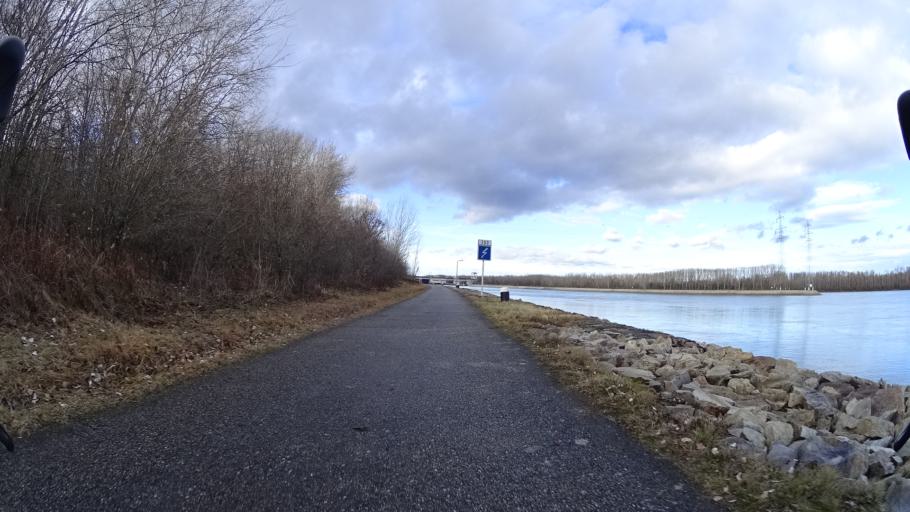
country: AT
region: Lower Austria
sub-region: Politischer Bezirk Tulln
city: Kirchberg am Wagram
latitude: 48.3700
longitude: 15.8704
